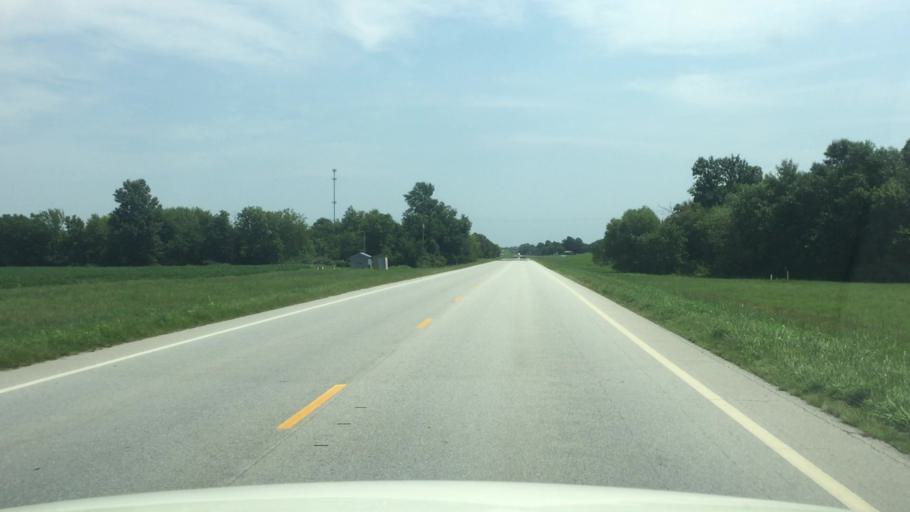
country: US
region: Kansas
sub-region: Cherokee County
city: Columbus
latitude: 37.1786
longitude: -94.8611
